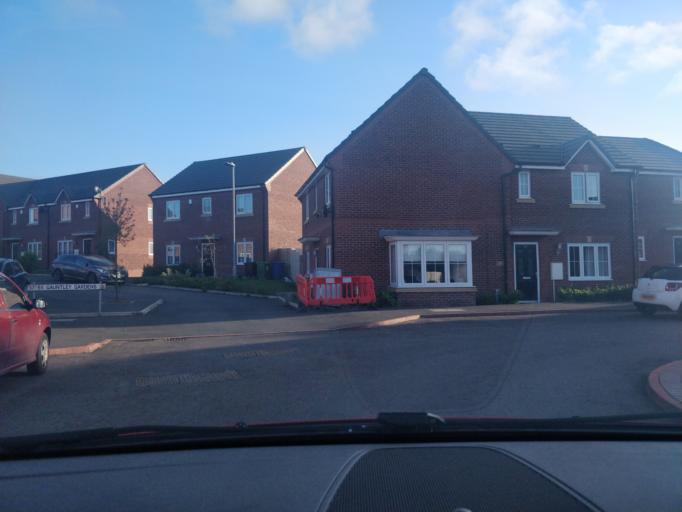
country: GB
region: England
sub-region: St. Helens
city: Billinge
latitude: 53.5201
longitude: -2.7230
